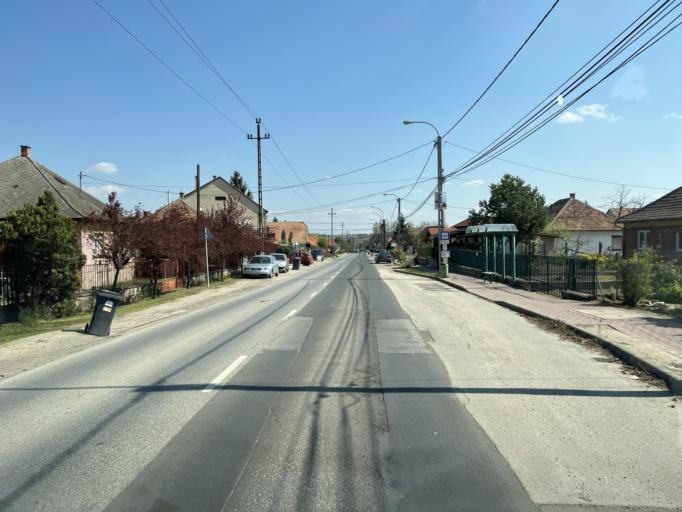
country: HU
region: Pest
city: Orbottyan
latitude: 47.6839
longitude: 19.2774
